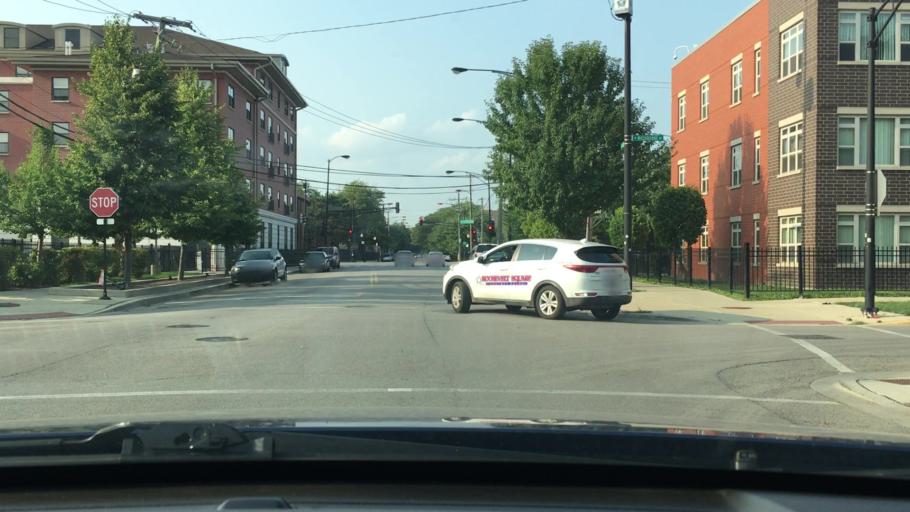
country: US
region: Illinois
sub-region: Cook County
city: Chicago
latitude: 41.8660
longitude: -87.6615
